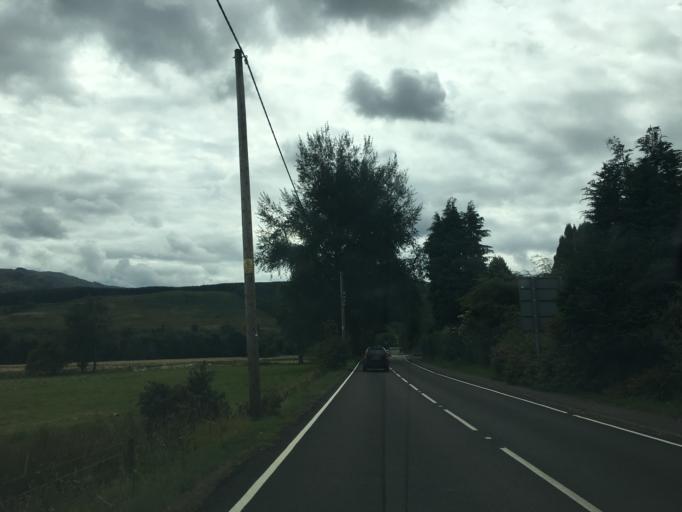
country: GB
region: Scotland
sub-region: Stirling
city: Callander
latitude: 56.3837
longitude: -4.2866
